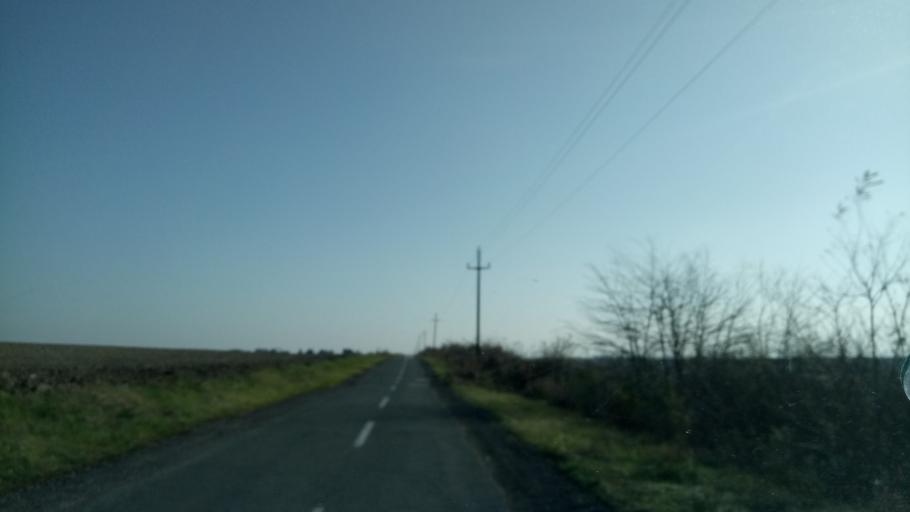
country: RS
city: Ljukovo
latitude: 45.0361
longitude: 20.0419
